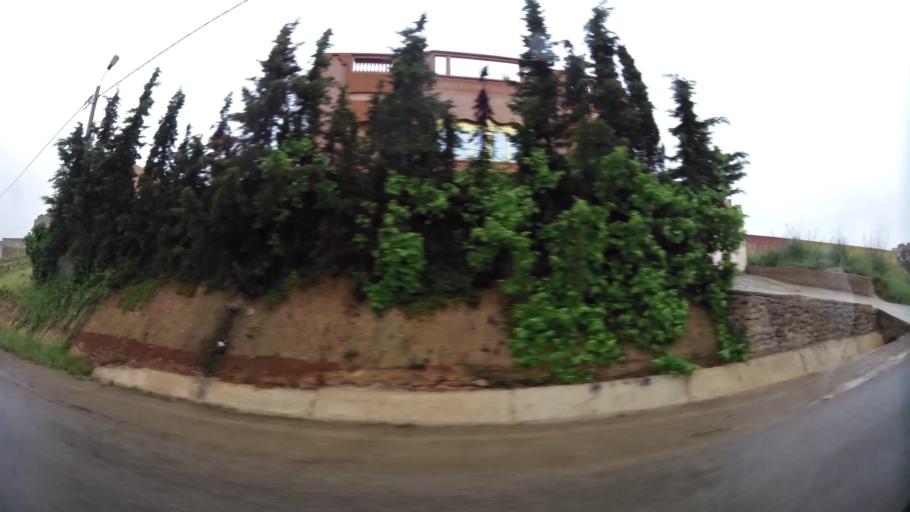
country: MA
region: Oriental
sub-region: Nador
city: Boudinar
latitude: 35.1291
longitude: -3.5832
